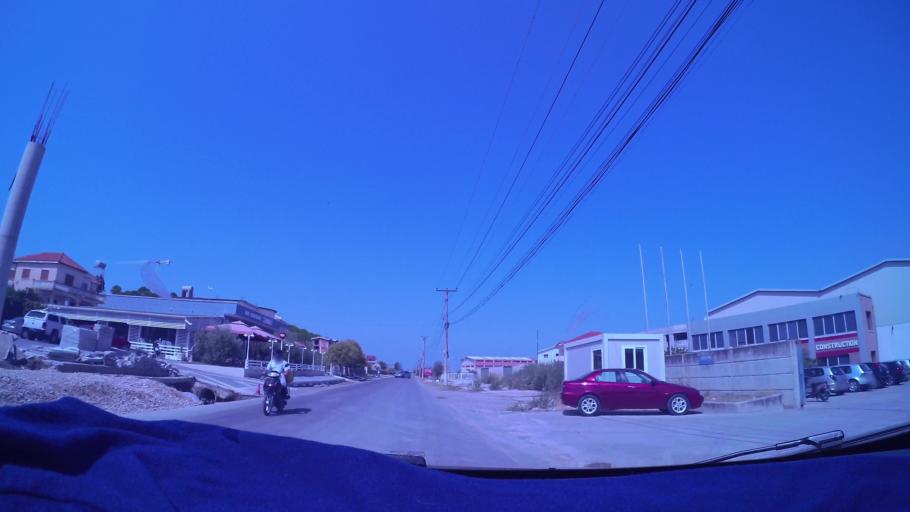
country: AL
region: Durres
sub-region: Rrethi i Durresit
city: Shijak
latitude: 41.3659
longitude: 19.5677
